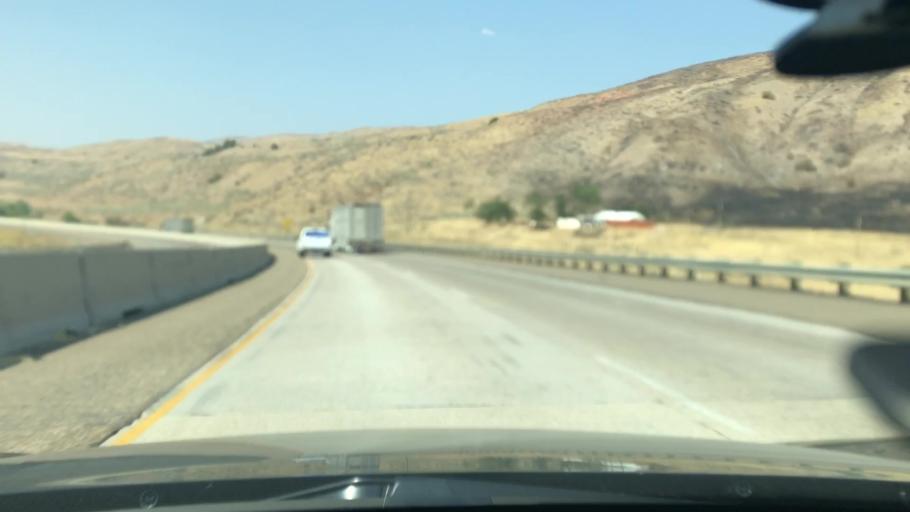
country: US
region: Idaho
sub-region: Washington County
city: Weiser
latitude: 44.4126
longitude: -117.3077
